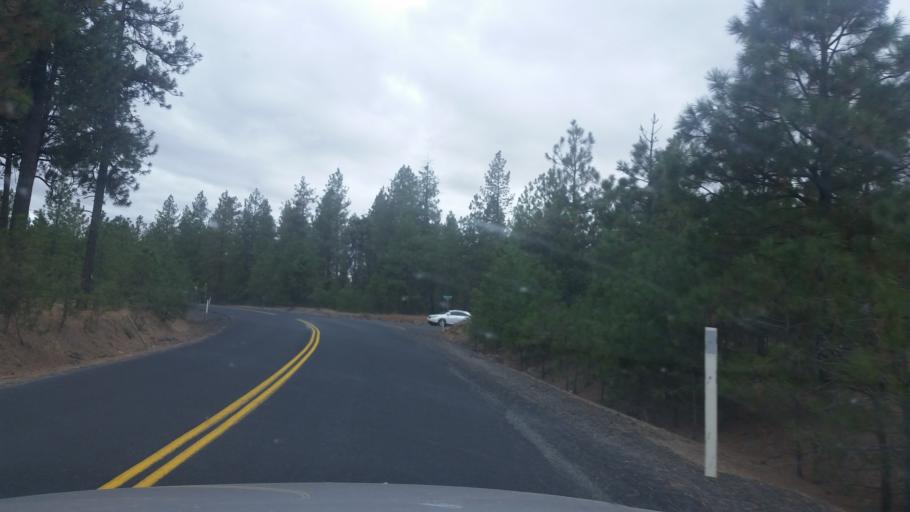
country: US
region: Washington
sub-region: Spokane County
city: Medical Lake
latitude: 47.5145
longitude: -117.7666
